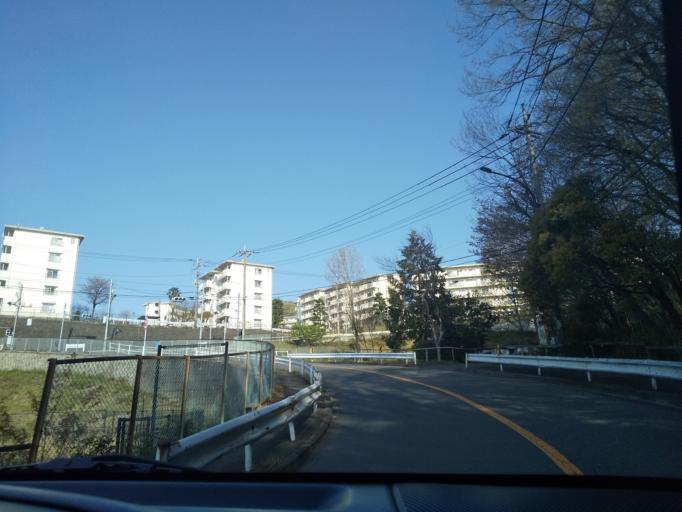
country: JP
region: Tokyo
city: Hino
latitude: 35.6461
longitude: 139.4195
